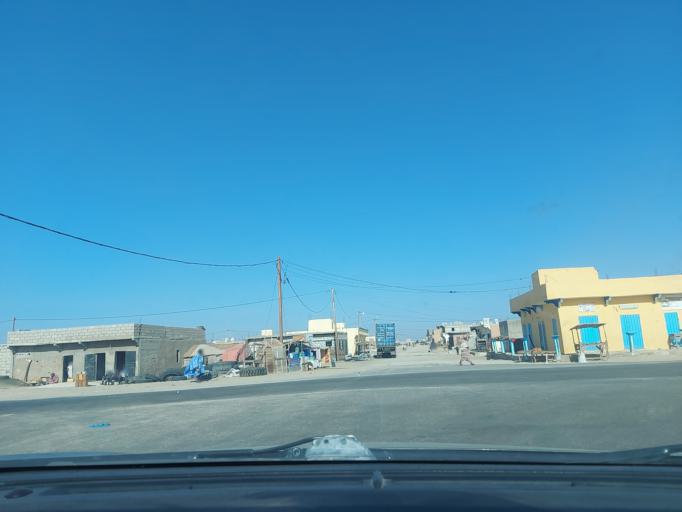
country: MR
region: Nouakchott
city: Nouakchott
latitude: 18.0118
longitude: -15.9871
